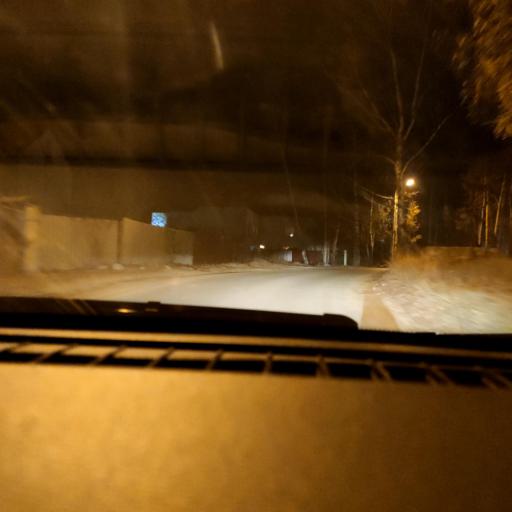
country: RU
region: Voronezj
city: Somovo
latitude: 51.7437
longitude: 39.3218
